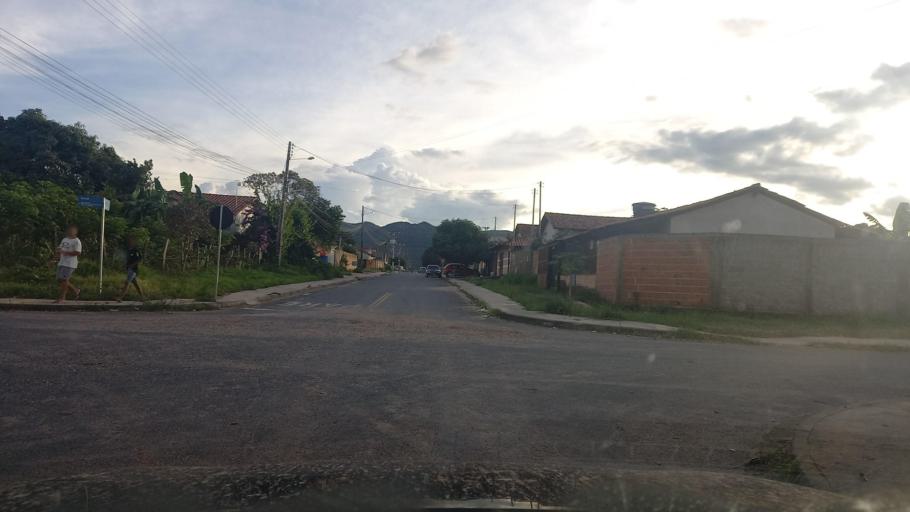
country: BR
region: Goias
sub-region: Cavalcante
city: Cavalcante
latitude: -13.7904
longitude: -47.4562
